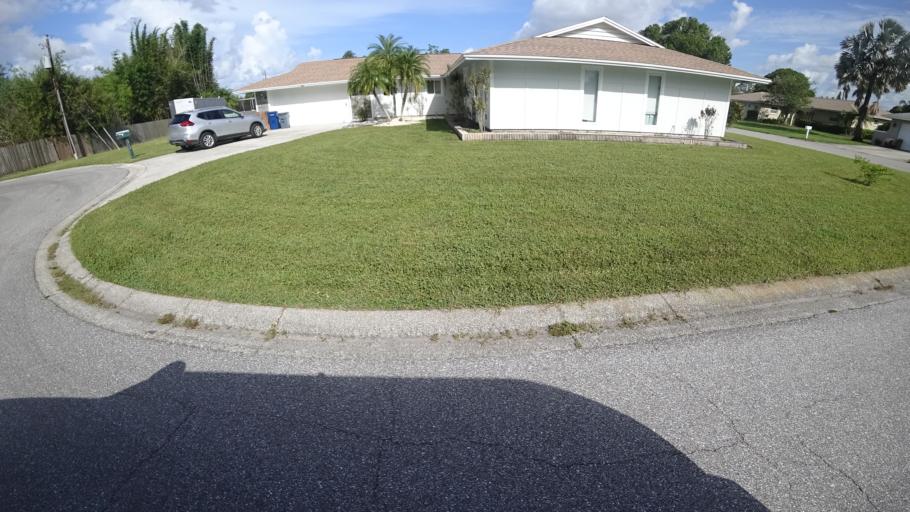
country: US
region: Florida
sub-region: Sarasota County
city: Desoto Lakes
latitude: 27.4031
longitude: -82.4960
